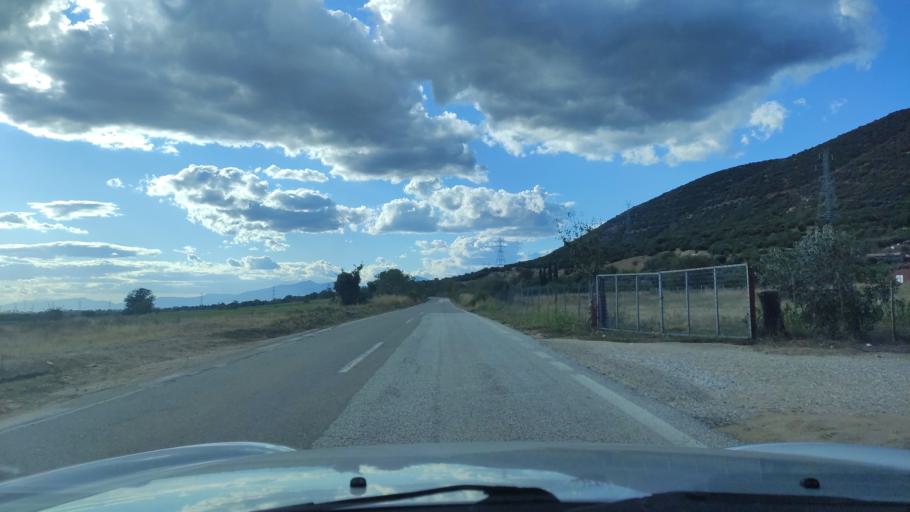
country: GR
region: East Macedonia and Thrace
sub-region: Nomos Rodopis
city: Iasmos
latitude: 41.1182
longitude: 25.1174
